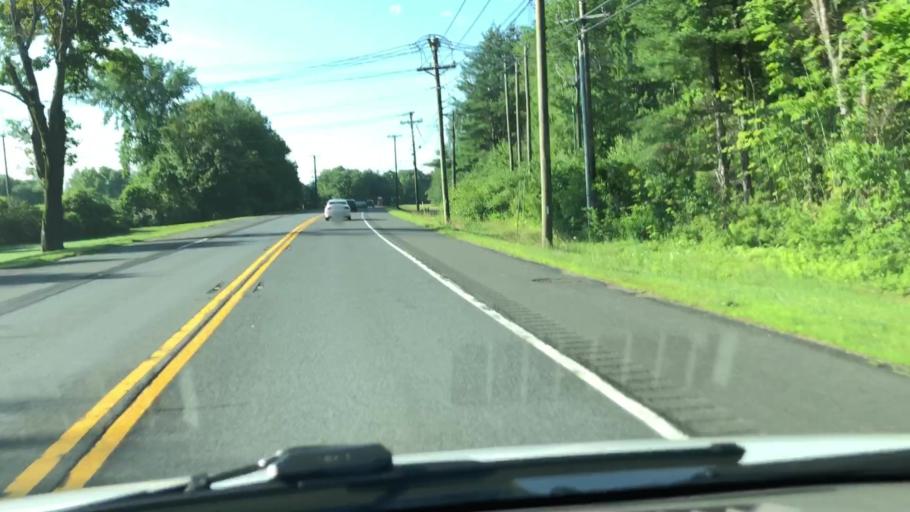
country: US
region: Massachusetts
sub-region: Hampshire County
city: North Amherst
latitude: 42.4246
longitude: -72.5385
